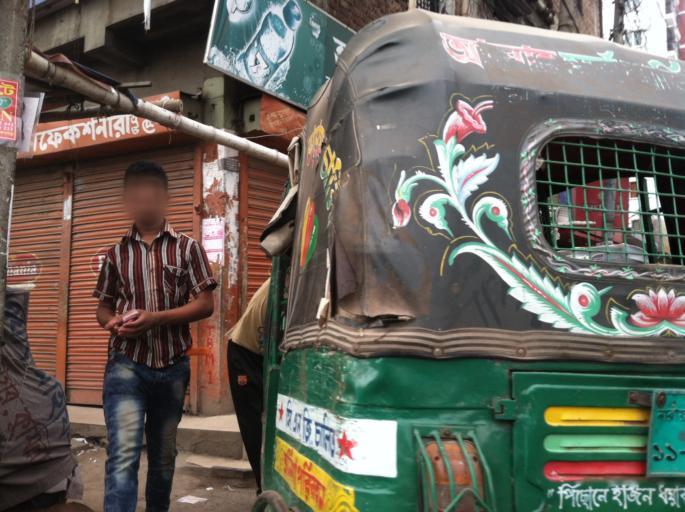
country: BD
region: Dhaka
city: Paltan
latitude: 23.7296
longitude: 90.4287
